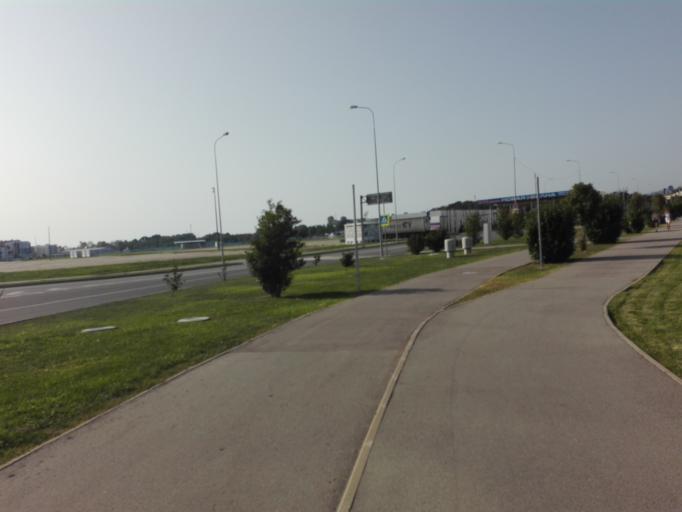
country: RU
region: Krasnodarskiy
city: Adler
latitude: 43.4117
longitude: 39.9494
